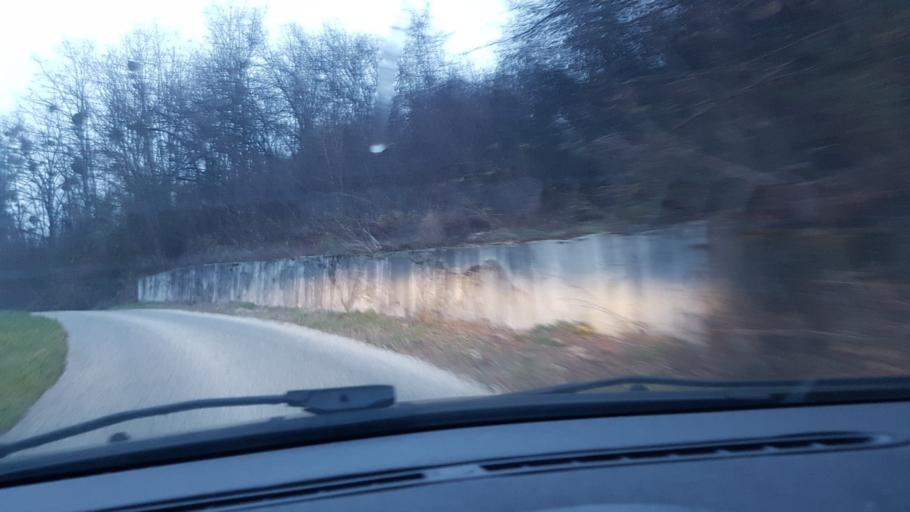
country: HR
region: Krapinsko-Zagorska
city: Pregrada
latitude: 46.1905
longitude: 15.7273
